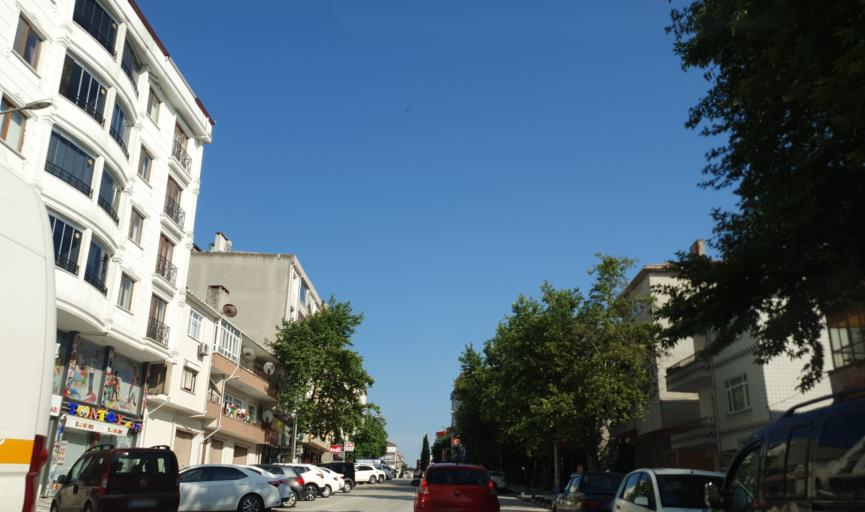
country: TR
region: Tekirdag
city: Saray
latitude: 41.4438
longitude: 27.9186
